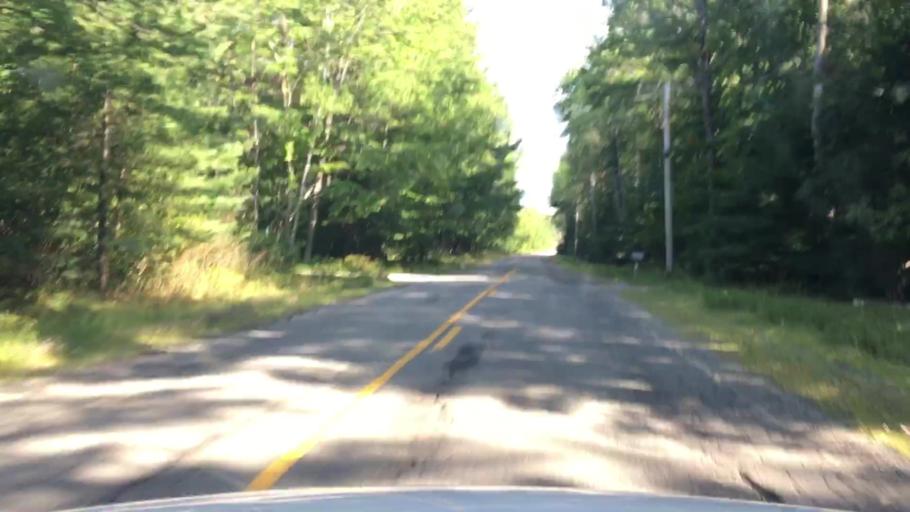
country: US
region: Maine
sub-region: Penobscot County
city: Enfield
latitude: 45.2173
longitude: -68.5331
